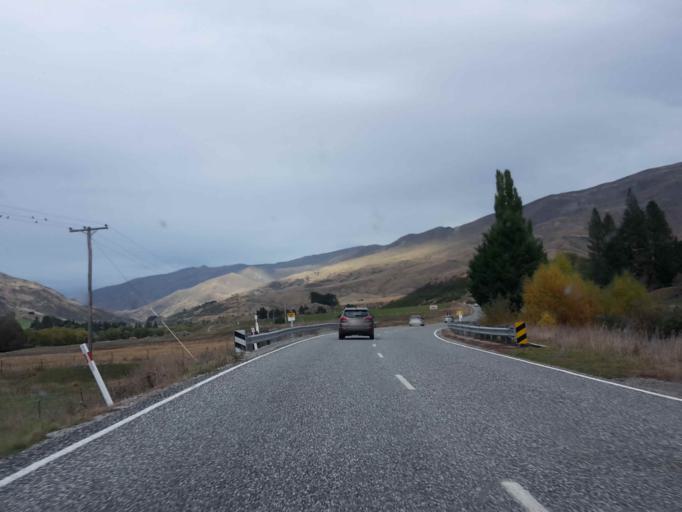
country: NZ
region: Otago
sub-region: Queenstown-Lakes District
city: Wanaka
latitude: -44.8553
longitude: 169.0324
